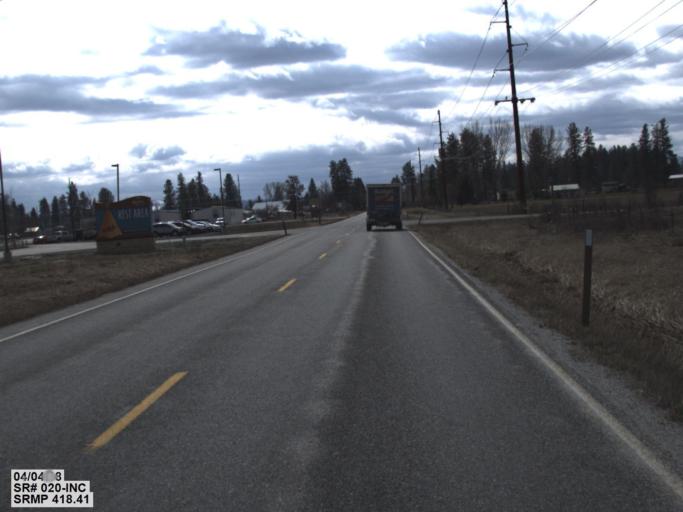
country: US
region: Washington
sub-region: Pend Oreille County
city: Newport
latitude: 48.3464
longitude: -117.3045
